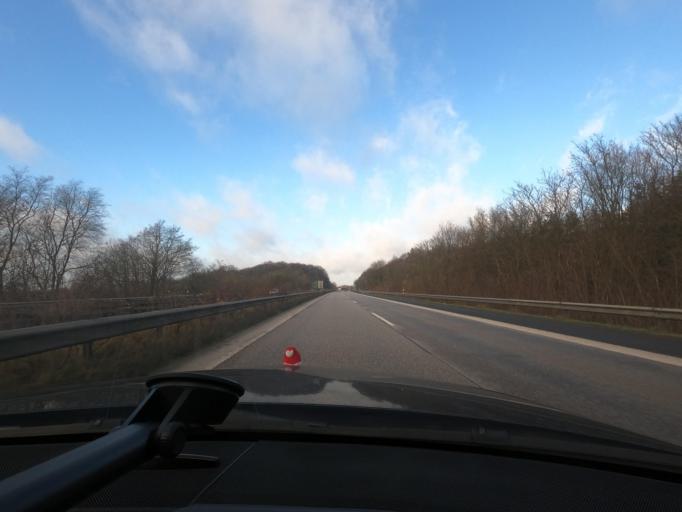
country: DE
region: Schleswig-Holstein
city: Neu Duvenstedt
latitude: 54.3727
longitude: 9.6633
